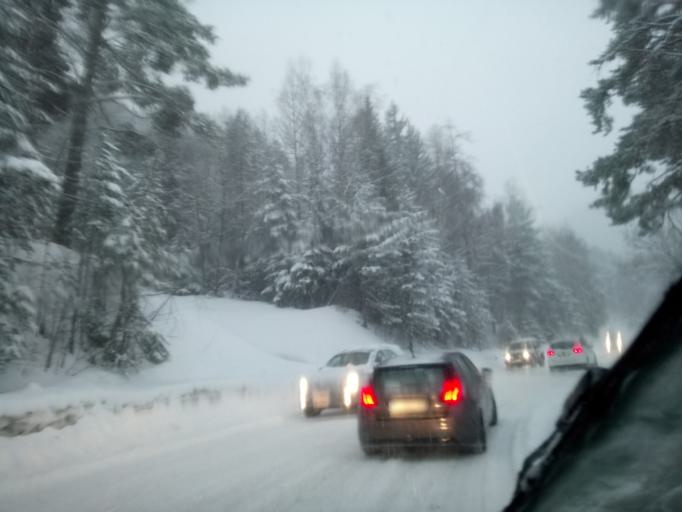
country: FR
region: Rhone-Alpes
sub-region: Departement de la Savoie
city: Modane
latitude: 45.2052
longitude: 6.7054
